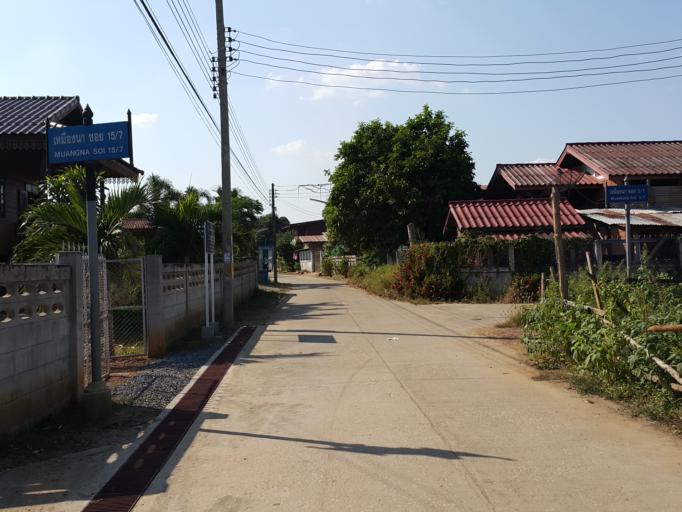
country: TH
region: Sukhothai
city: Thung Saliam
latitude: 17.3167
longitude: 99.5618
